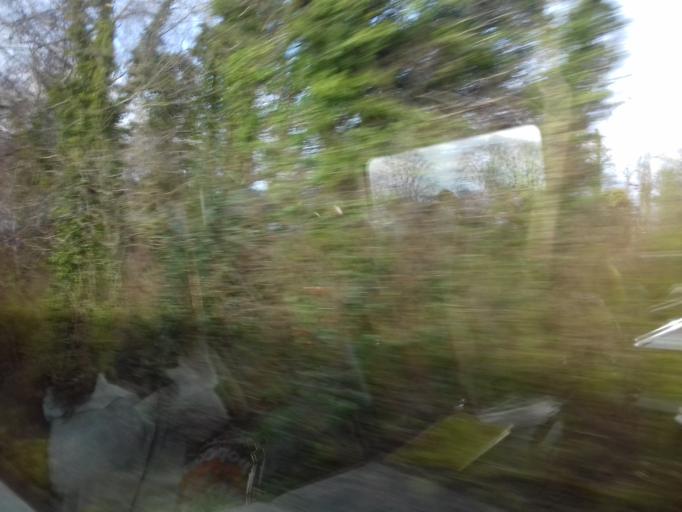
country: IE
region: Leinster
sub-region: An Mhi
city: Longwood
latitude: 53.4572
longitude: -6.9634
